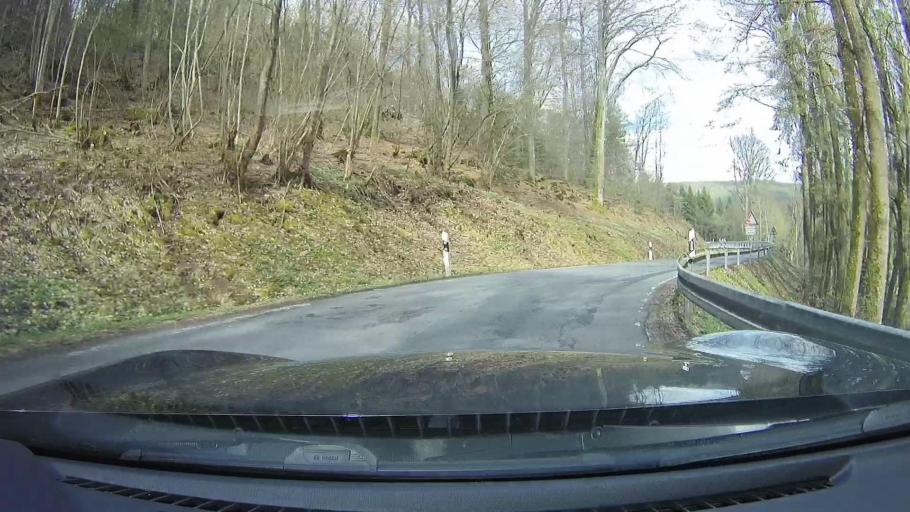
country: DE
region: Bavaria
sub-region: Regierungsbezirk Unterfranken
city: Kirchzell
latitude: 49.6266
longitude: 9.1152
